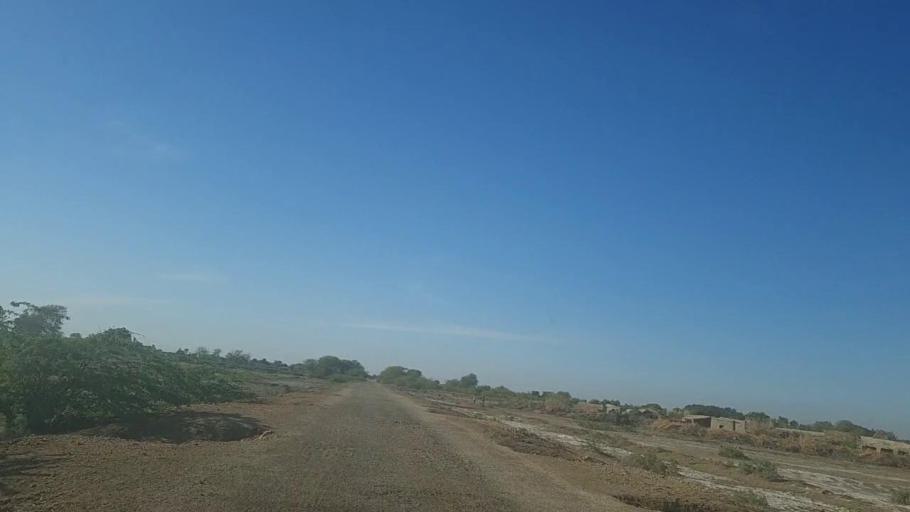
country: PK
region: Sindh
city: Pithoro
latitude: 25.5134
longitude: 69.3871
